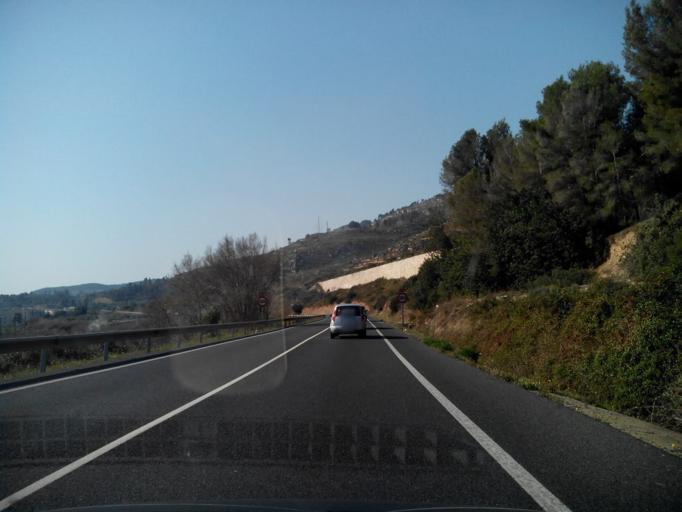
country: ES
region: Catalonia
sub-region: Provincia de Tarragona
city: Alcover
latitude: 41.2991
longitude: 1.1954
